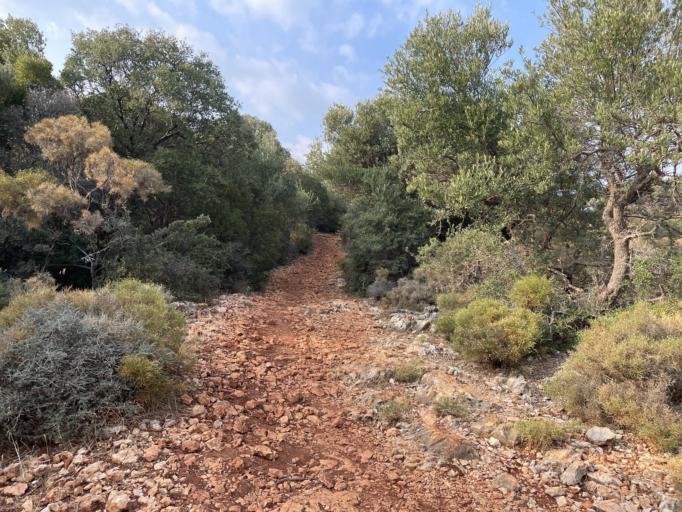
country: TR
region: Antalya
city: Kas
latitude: 36.1626
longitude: 29.6548
